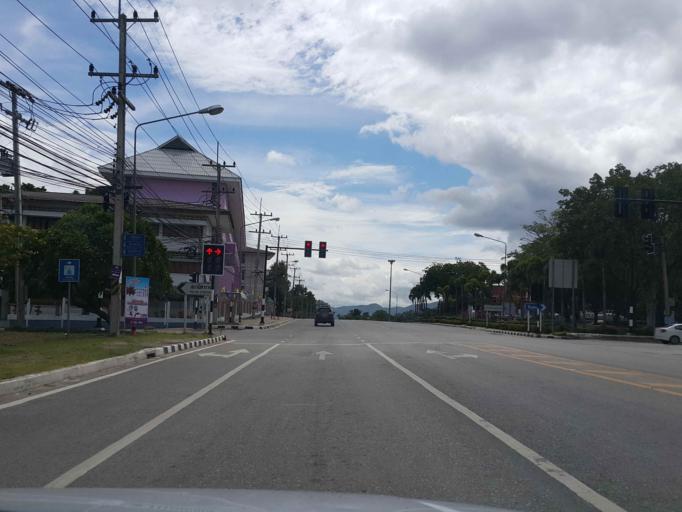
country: TH
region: Tak
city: Tak
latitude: 16.8858
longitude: 99.1227
